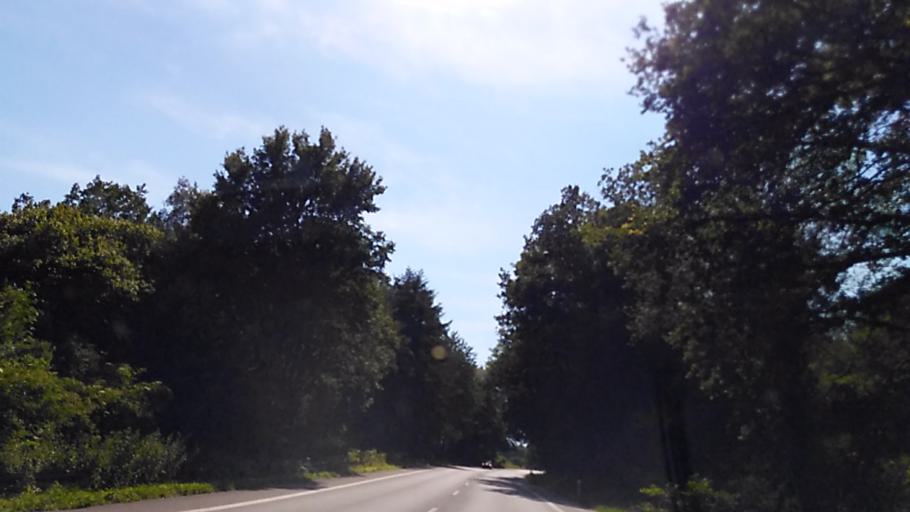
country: DE
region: North Rhine-Westphalia
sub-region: Regierungsbezirk Arnsberg
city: Hagen
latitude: 51.3506
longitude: 7.5355
